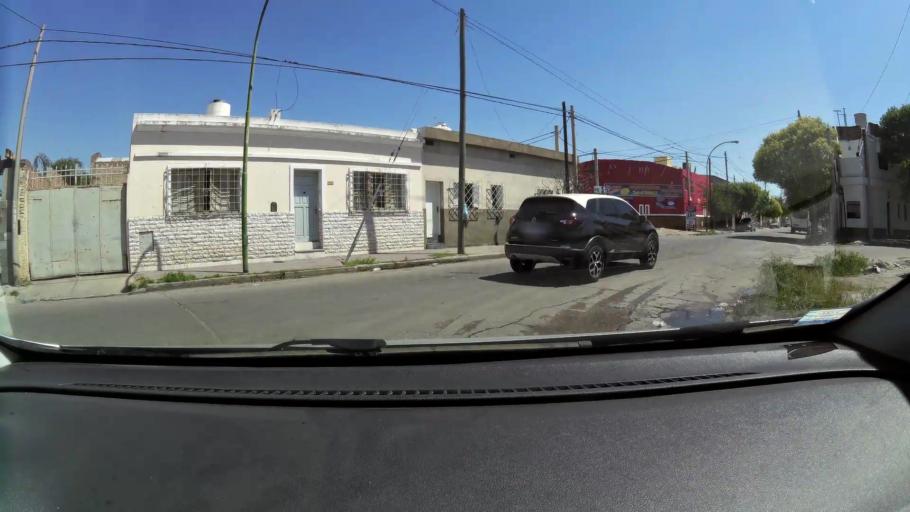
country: AR
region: Cordoba
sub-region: Departamento de Capital
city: Cordoba
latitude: -31.3819
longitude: -64.1497
